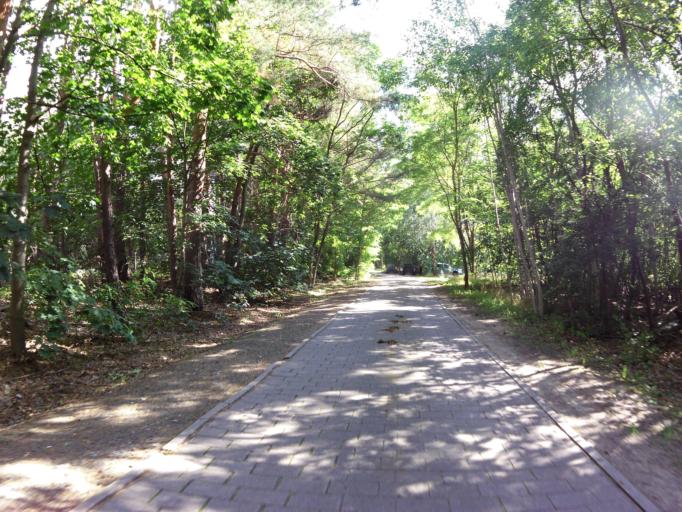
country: DE
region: Brandenburg
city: Munchehofe
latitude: 52.1902
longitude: 13.8800
